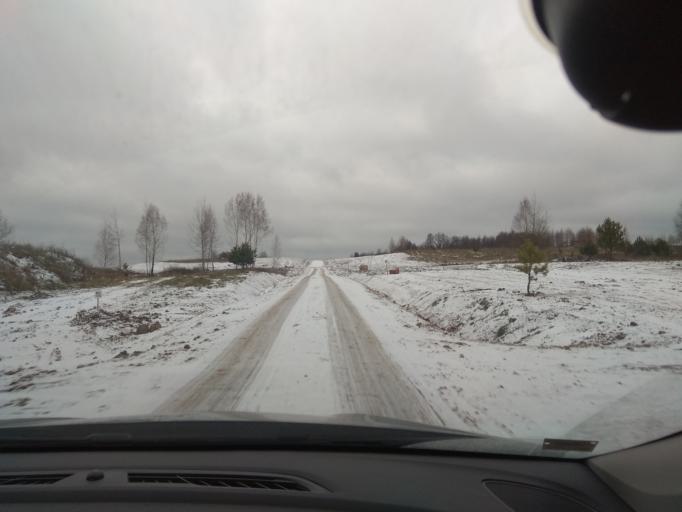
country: LT
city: Lentvaris
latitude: 54.6457
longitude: 25.0829
